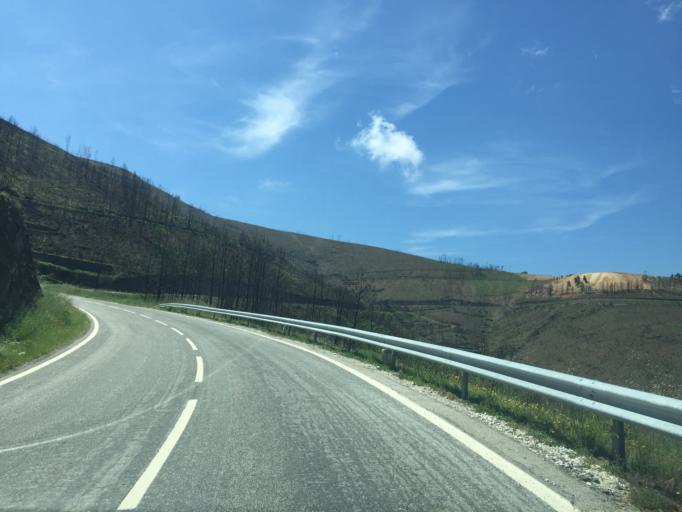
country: PT
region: Coimbra
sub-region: Pampilhosa da Serra
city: Pampilhosa da Serra
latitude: 40.0346
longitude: -7.9599
